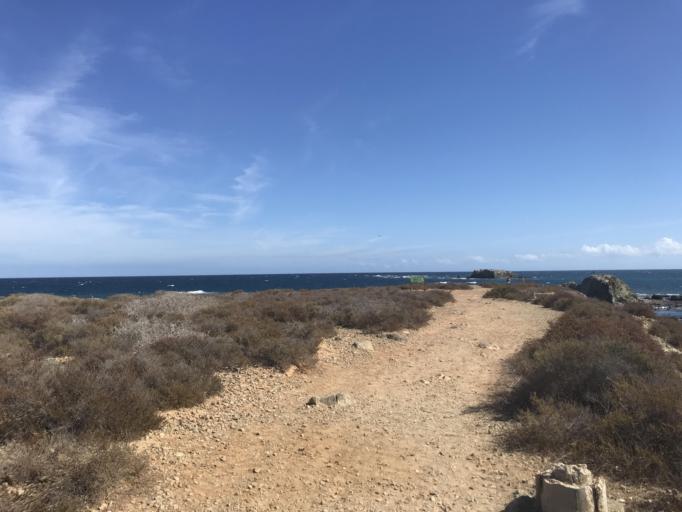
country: ES
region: Valencia
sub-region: Provincia de Alicante
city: Santa Pola
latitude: 38.1634
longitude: -0.4659
